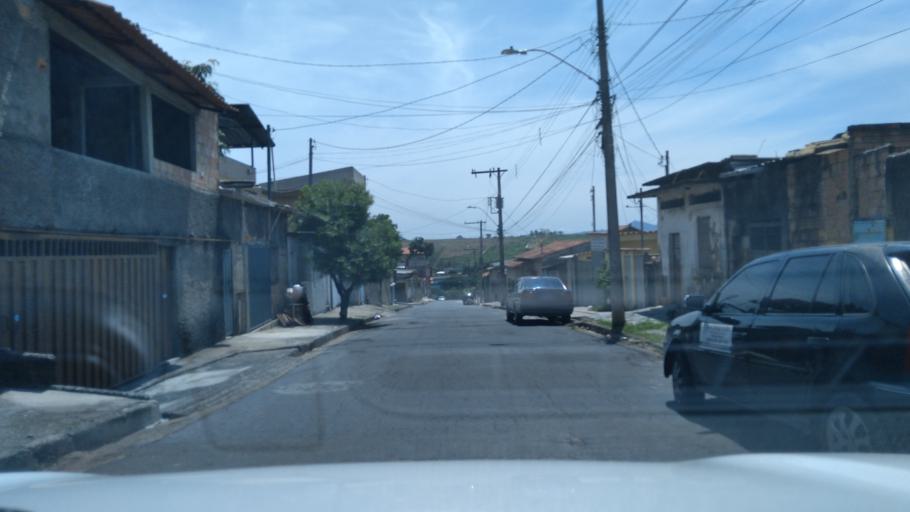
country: BR
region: Minas Gerais
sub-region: Contagem
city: Contagem
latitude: -19.9098
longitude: -44.0254
